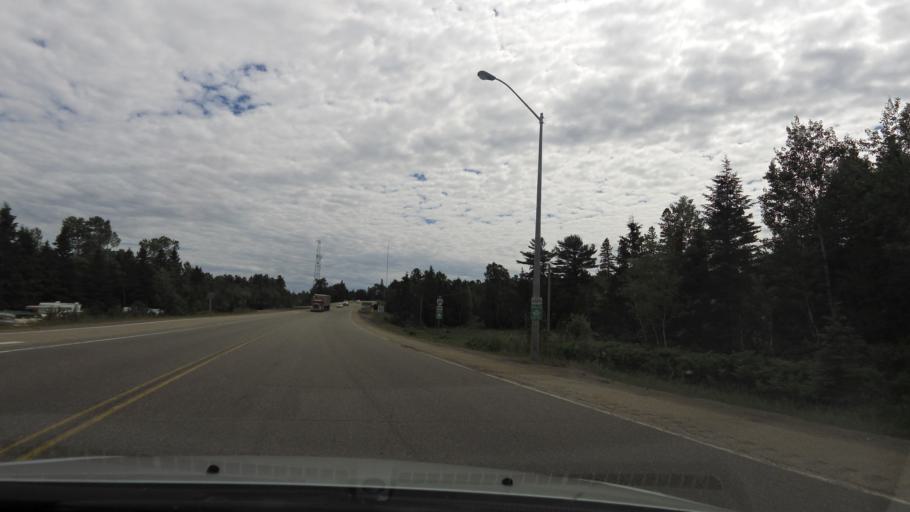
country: CA
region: Ontario
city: Greater Sudbury
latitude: 45.9135
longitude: -80.5732
